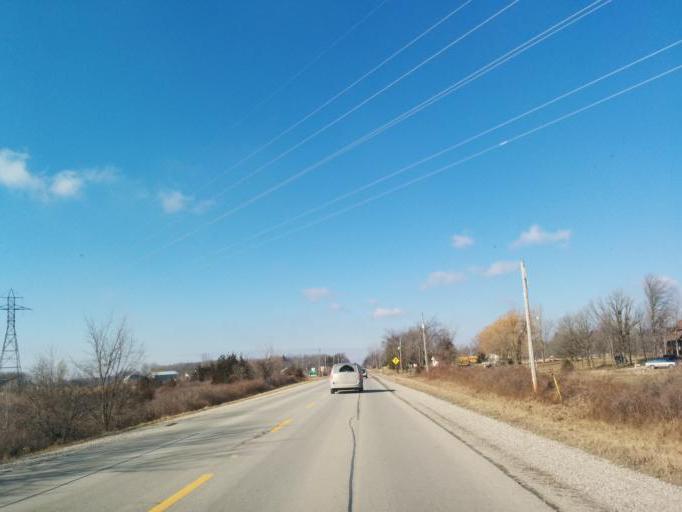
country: CA
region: Ontario
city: Brantford
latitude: 43.0103
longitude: -80.1825
